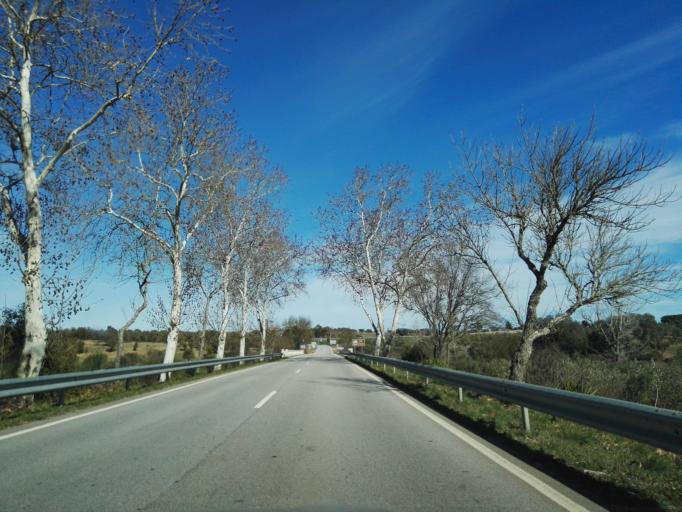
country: PT
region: Portalegre
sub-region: Arronches
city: Arronches
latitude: 39.1302
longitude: -7.2934
